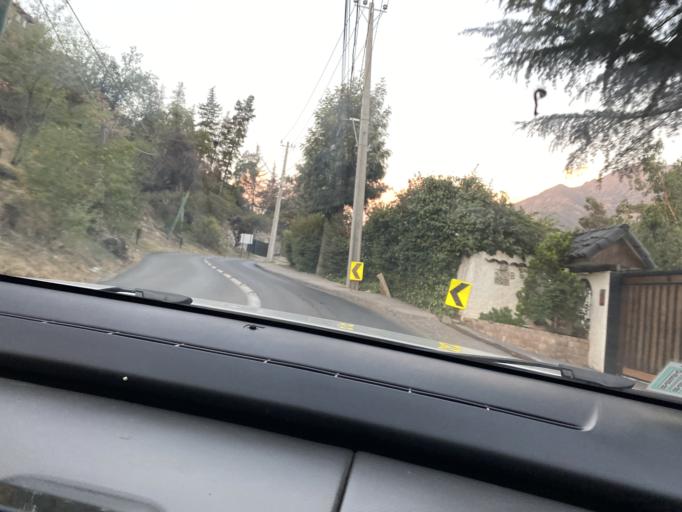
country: CL
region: Santiago Metropolitan
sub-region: Provincia de Santiago
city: Villa Presidente Frei, Nunoa, Santiago, Chile
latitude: -33.3619
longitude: -70.4883
